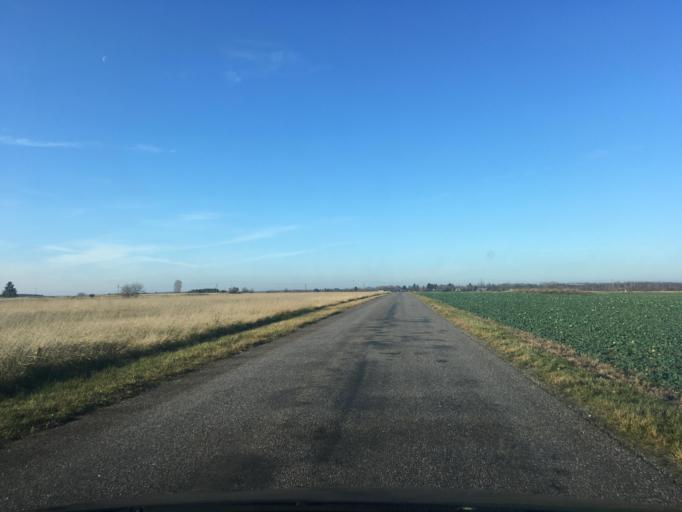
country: EE
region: Harju
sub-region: Maardu linn
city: Maardu
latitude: 59.4515
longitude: 25.1128
